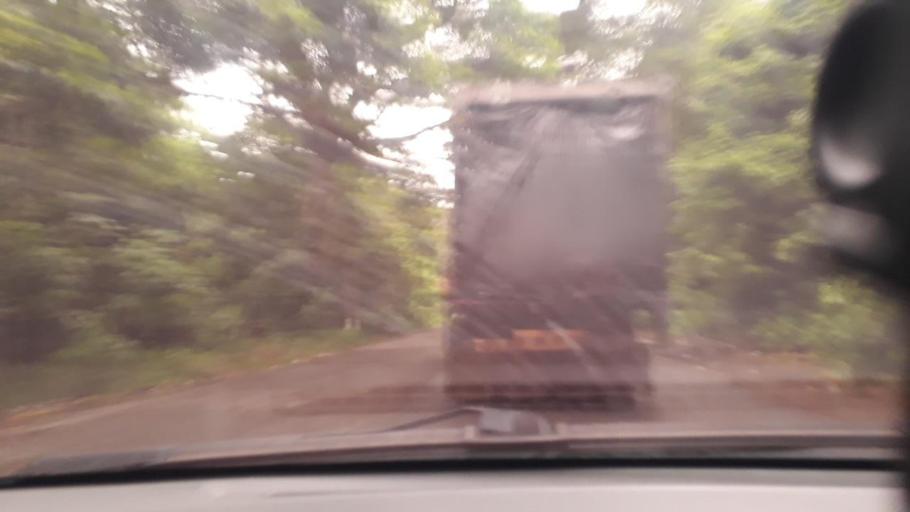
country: GT
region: Jutiapa
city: Asuncion Mita
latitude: 14.2512
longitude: -89.7142
